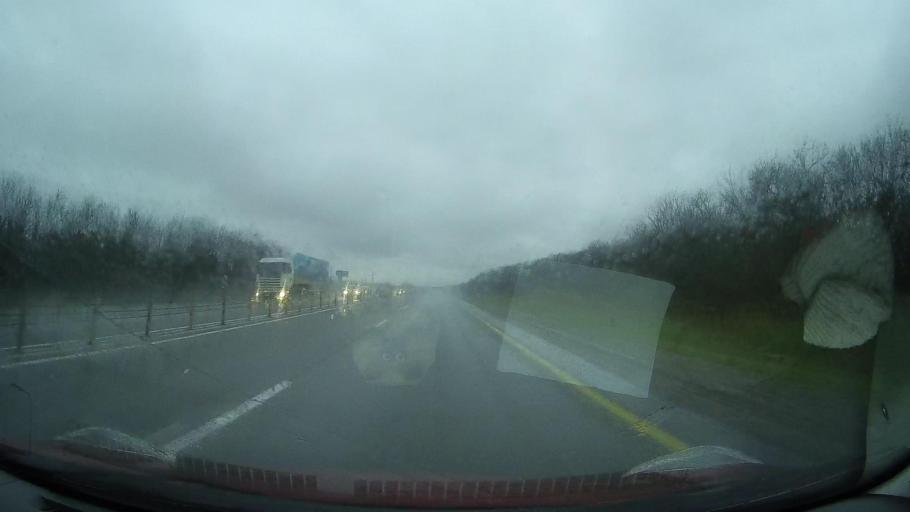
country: RU
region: Stavropol'skiy
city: Nevinnomyssk
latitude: 44.6392
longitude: 41.9776
